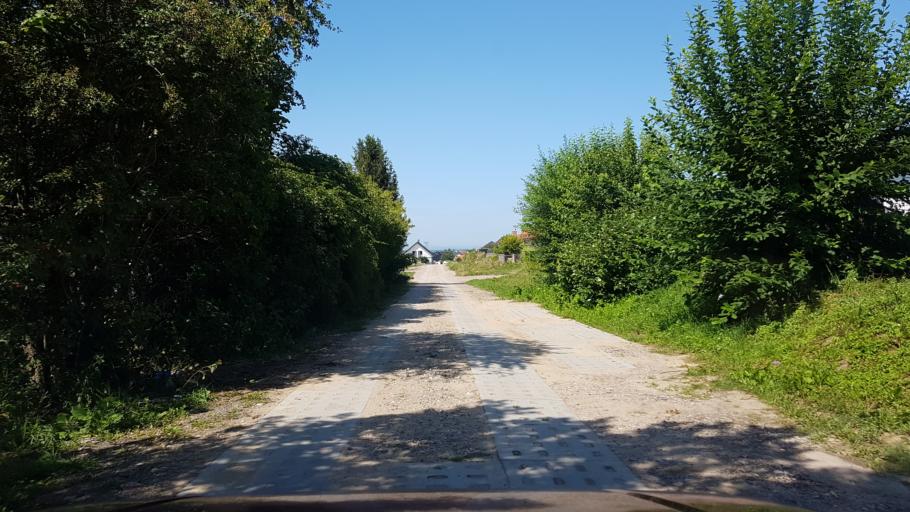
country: PL
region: West Pomeranian Voivodeship
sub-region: Koszalin
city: Koszalin
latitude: 54.2151
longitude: 16.1714
